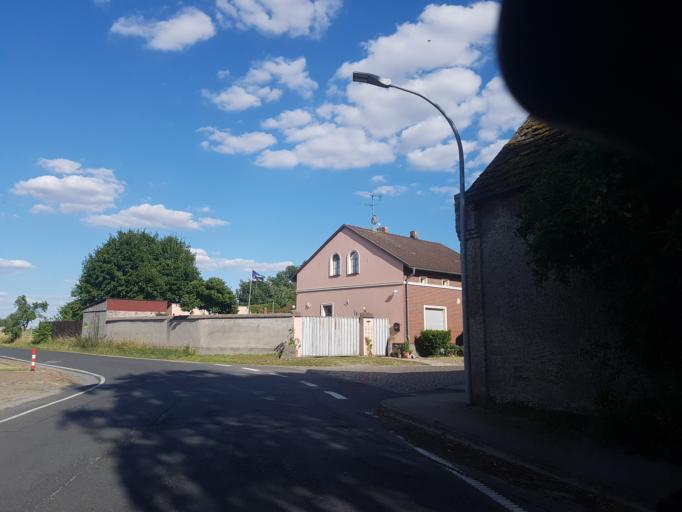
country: DE
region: Brandenburg
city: Juterbog
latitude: 51.9292
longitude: 13.1389
